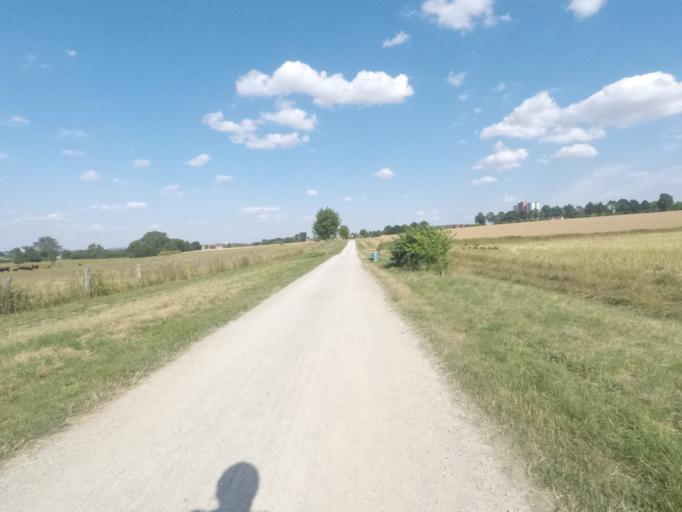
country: DE
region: North Rhine-Westphalia
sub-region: Regierungsbezirk Detmold
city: Bielefeld
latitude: 52.0543
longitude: 8.5837
